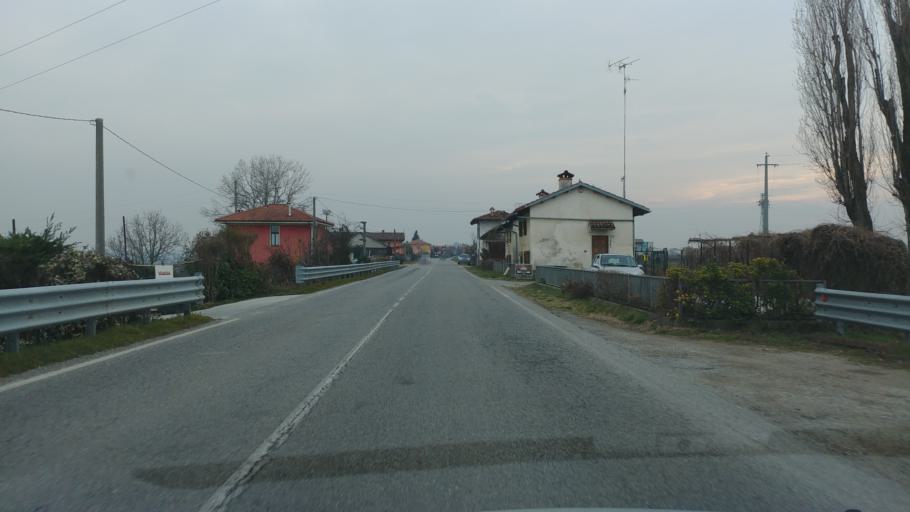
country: IT
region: Piedmont
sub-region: Provincia di Cuneo
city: Sant'Albano Stura
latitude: 44.5267
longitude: 7.7055
